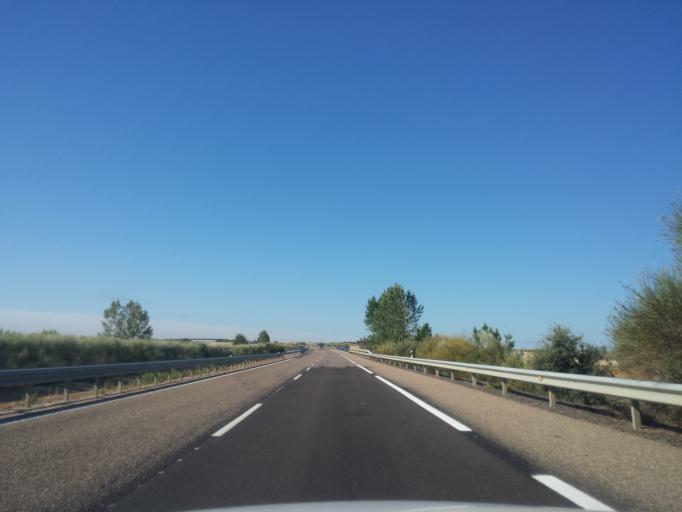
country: ES
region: Castille and Leon
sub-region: Provincia de Zamora
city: Matilla de Arzon
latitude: 42.1186
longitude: -5.6554
